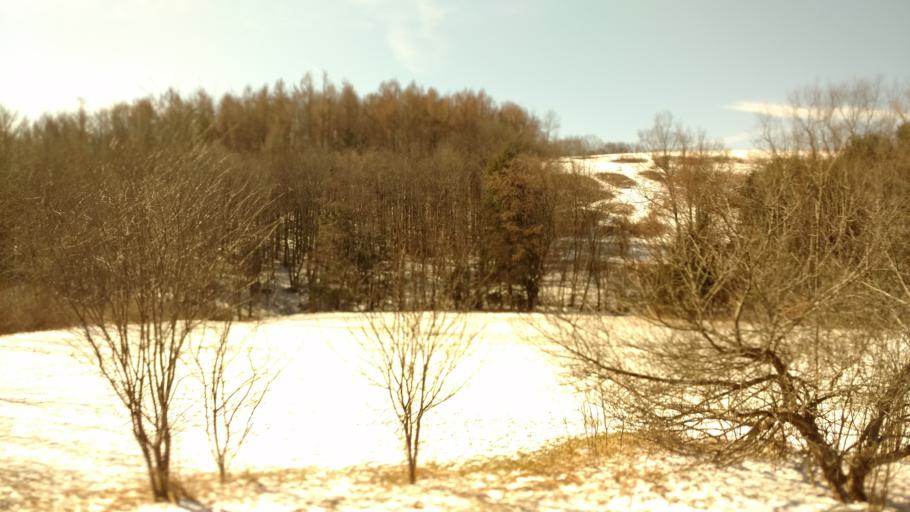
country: US
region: New York
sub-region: Allegany County
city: Wellsville
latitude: 42.0834
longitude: -77.9754
